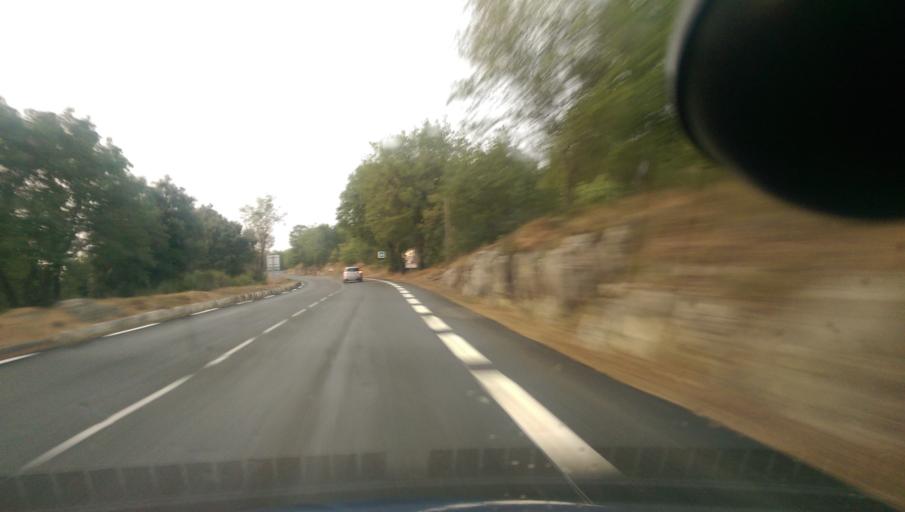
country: FR
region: Provence-Alpes-Cote d'Azur
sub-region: Departement des Alpes-Maritimes
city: Grasse
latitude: 43.6679
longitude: 6.9155
